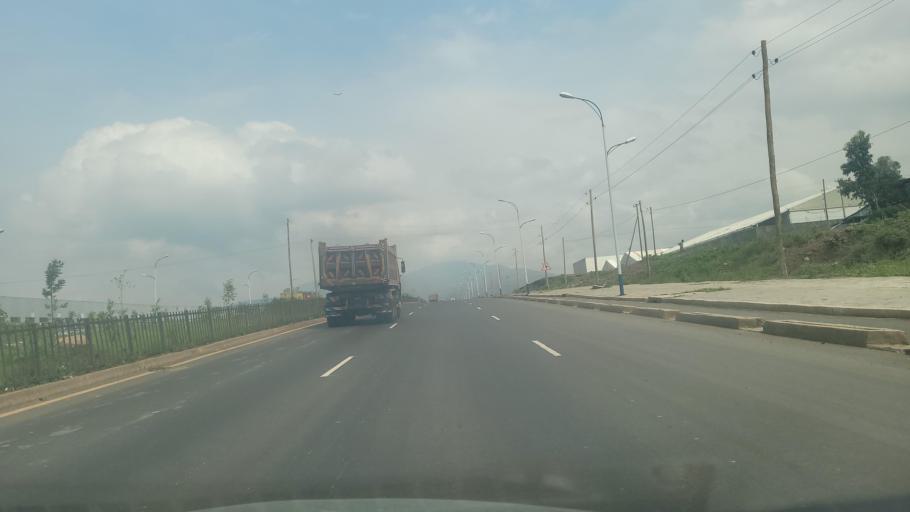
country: ET
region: Adis Abeba
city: Addis Ababa
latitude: 8.9498
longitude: 38.7068
